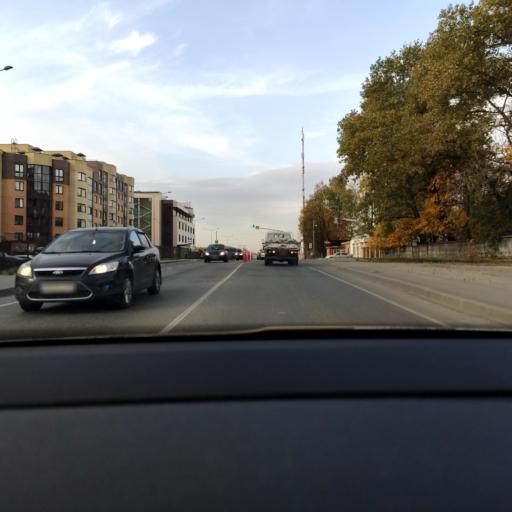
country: RU
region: Moskovskaya
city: Pirogovskiy
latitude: 55.9638
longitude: 37.6685
